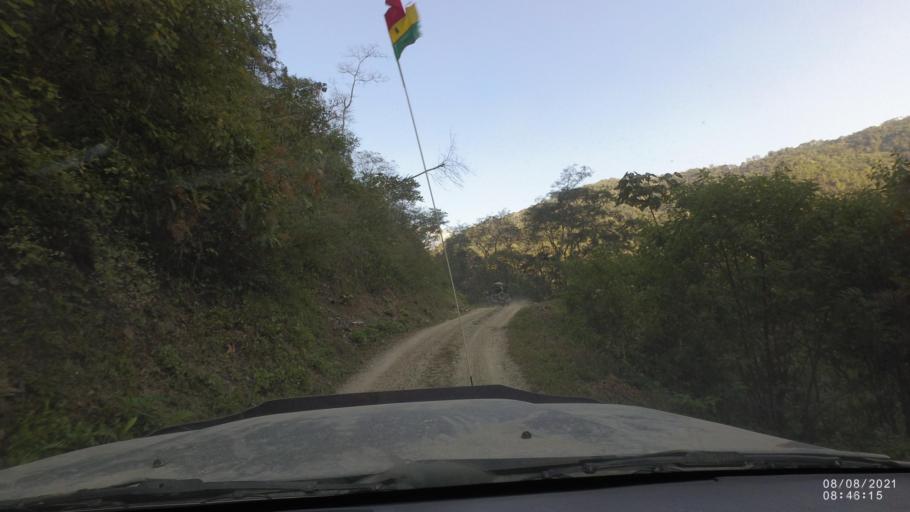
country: BO
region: La Paz
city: Quime
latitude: -16.5259
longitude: -66.7515
